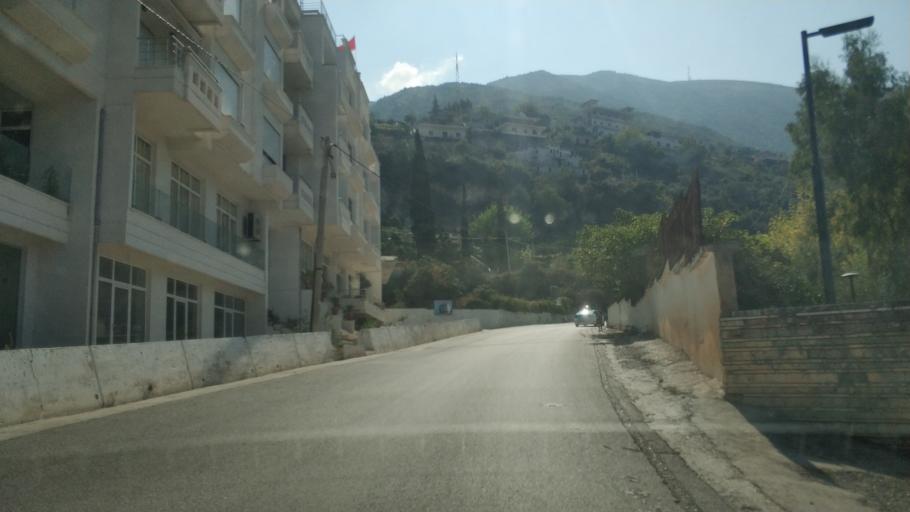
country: AL
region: Vlore
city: Vlore
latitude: 40.4184
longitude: 19.4872
